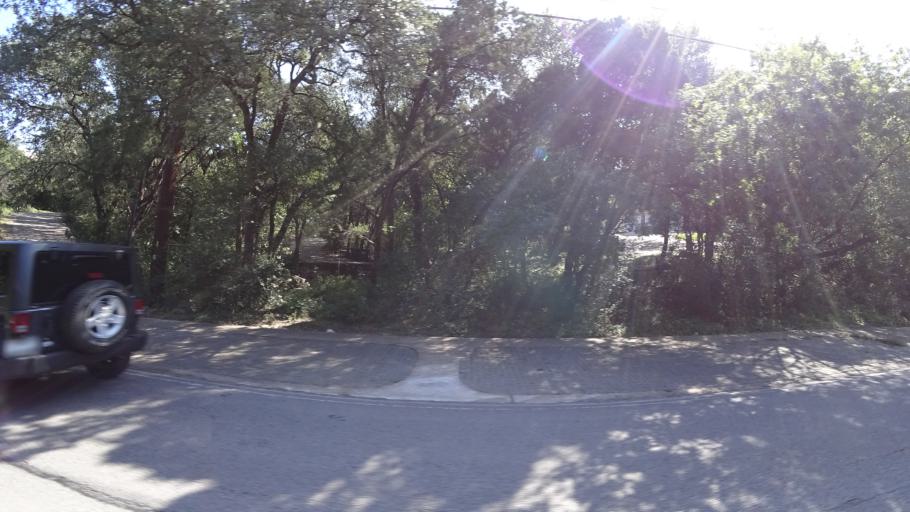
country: US
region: Texas
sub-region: Travis County
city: West Lake Hills
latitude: 30.2913
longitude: -97.8008
